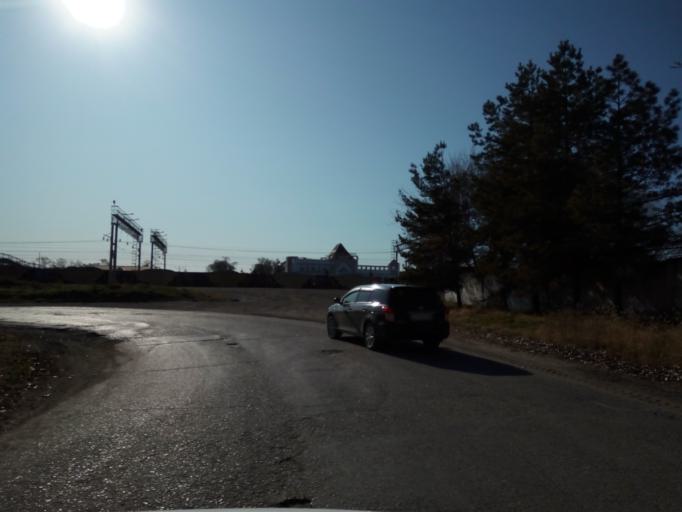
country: RU
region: Primorskiy
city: Dal'nerechensk
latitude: 45.9366
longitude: 133.7236
